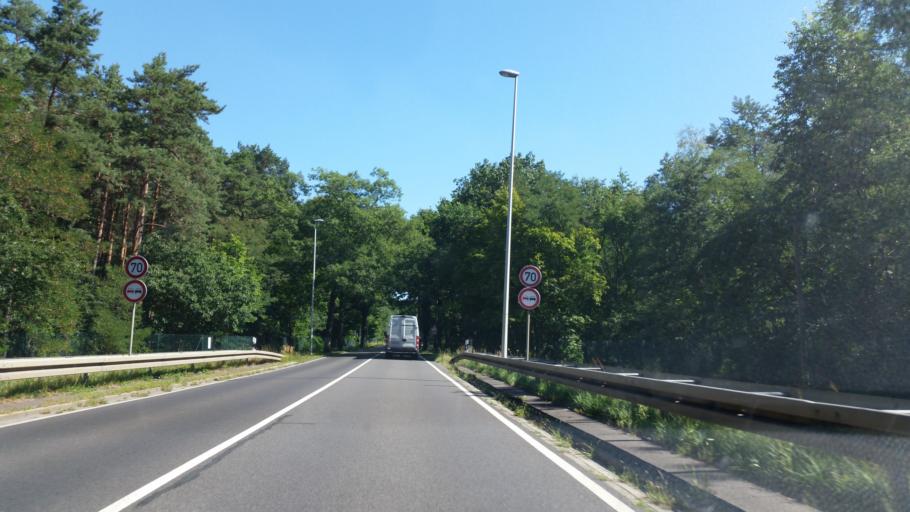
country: DE
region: Brandenburg
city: Cottbus
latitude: 51.7256
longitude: 14.3032
